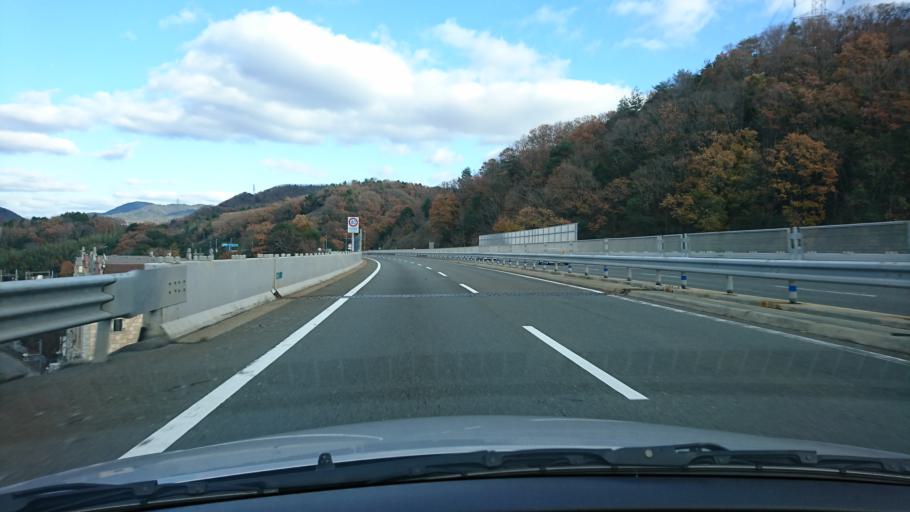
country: JP
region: Hyogo
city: Kobe
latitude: 34.7553
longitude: 135.1521
